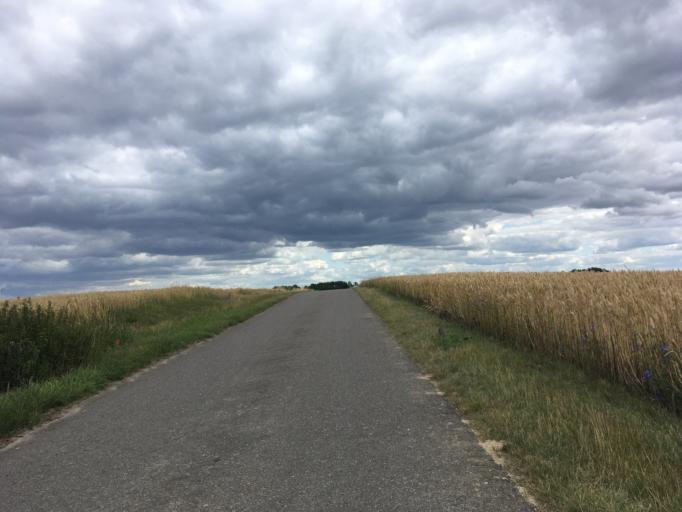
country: DE
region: Brandenburg
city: Gramzow
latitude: 53.2550
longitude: 13.9894
